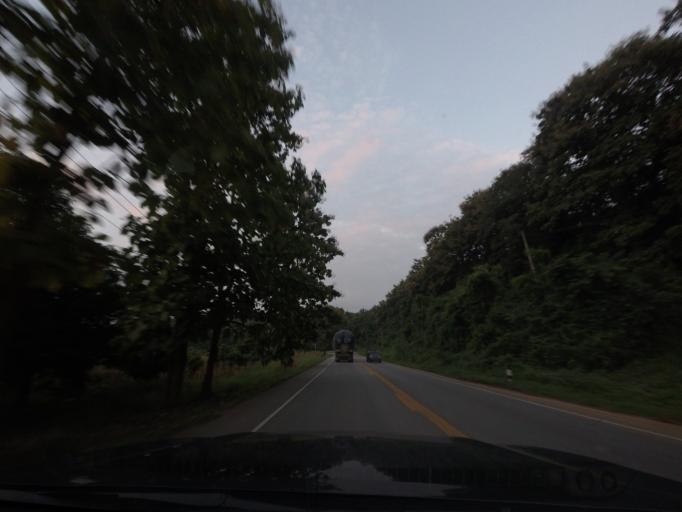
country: TH
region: Nan
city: Wiang Sa
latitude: 18.4735
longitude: 100.7234
